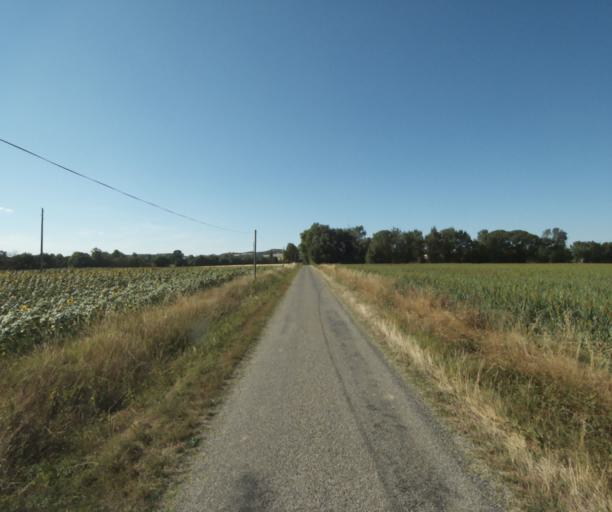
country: FR
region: Midi-Pyrenees
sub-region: Departement de la Haute-Garonne
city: Revel
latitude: 43.4764
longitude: 1.9590
